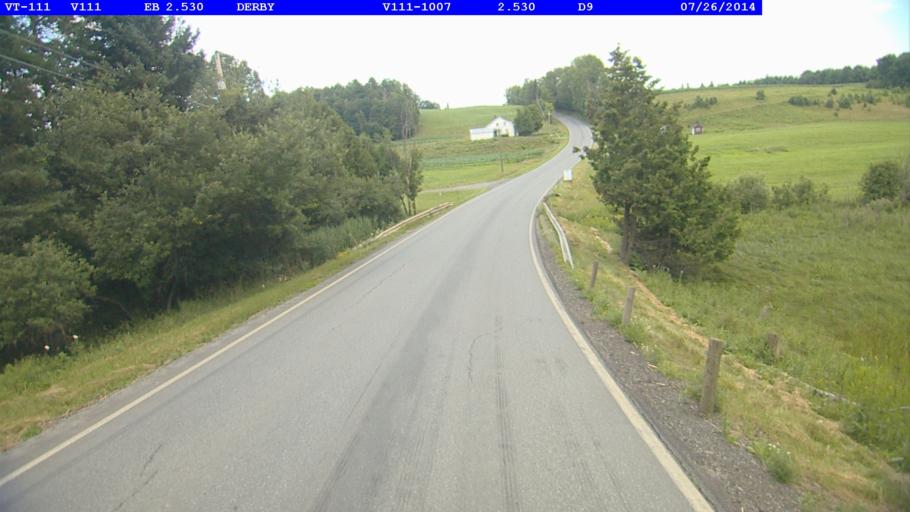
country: US
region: Vermont
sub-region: Orleans County
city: Newport
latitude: 44.9382
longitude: -72.0891
